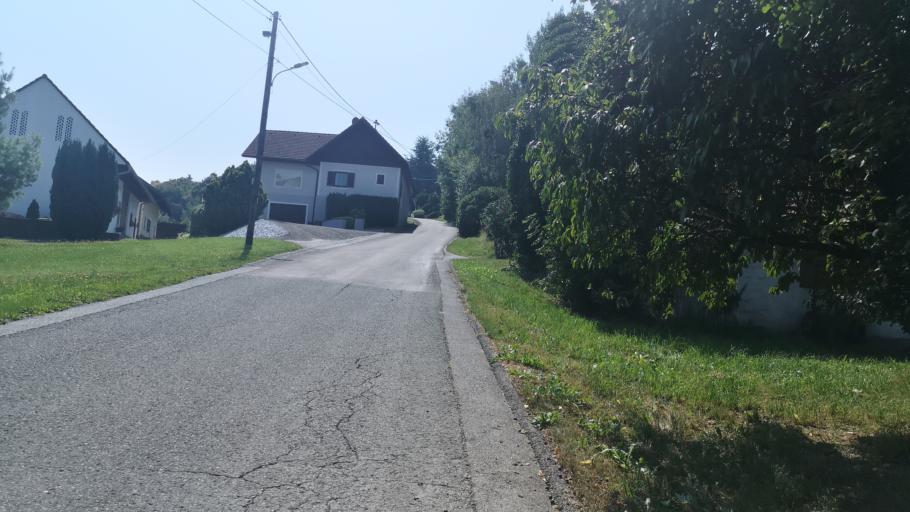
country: AT
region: Styria
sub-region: Politischer Bezirk Deutschlandsberg
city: Lannach
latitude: 46.9319
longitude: 15.3519
